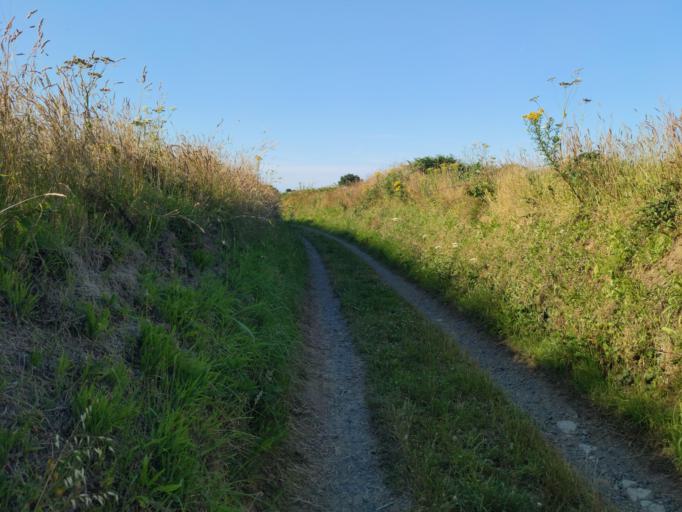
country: FR
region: Brittany
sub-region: Departement des Cotes-d'Armor
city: Pleubian
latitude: 48.8438
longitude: -3.1402
